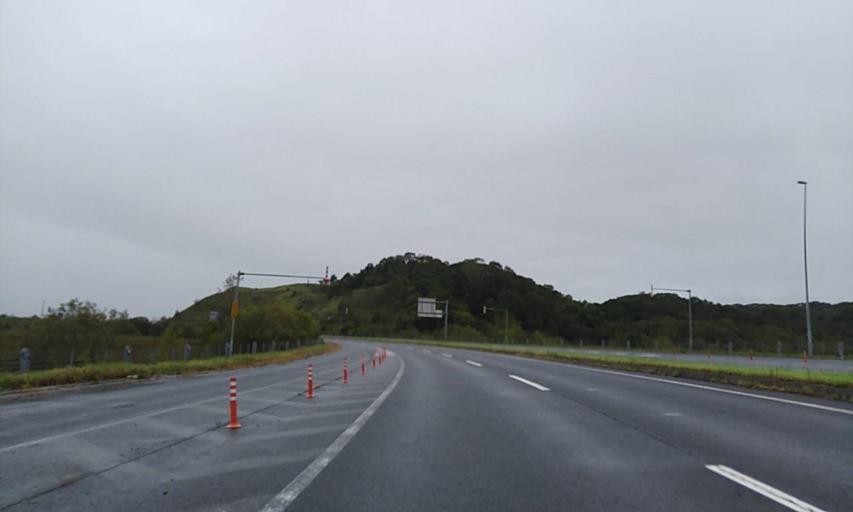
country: JP
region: Hokkaido
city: Kushiro
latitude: 43.0196
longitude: 144.2583
